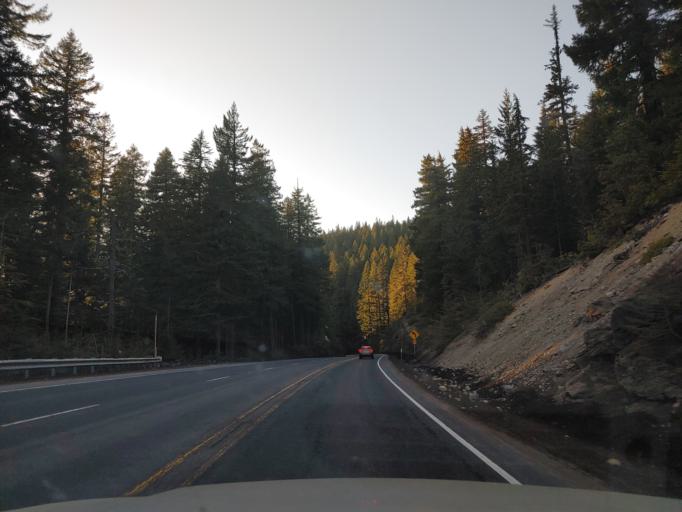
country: US
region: Oregon
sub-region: Lane County
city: Oakridge
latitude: 43.6119
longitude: -122.1250
